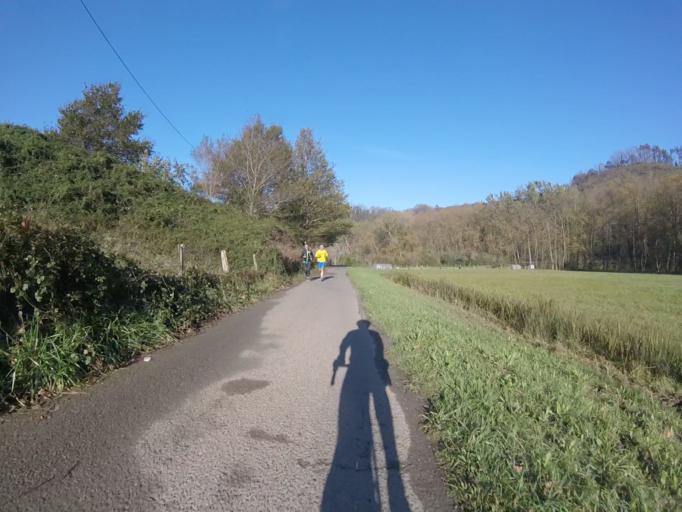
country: ES
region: Basque Country
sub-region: Provincia de Guipuzcoa
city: Usurbil
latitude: 43.2765
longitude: -2.0601
